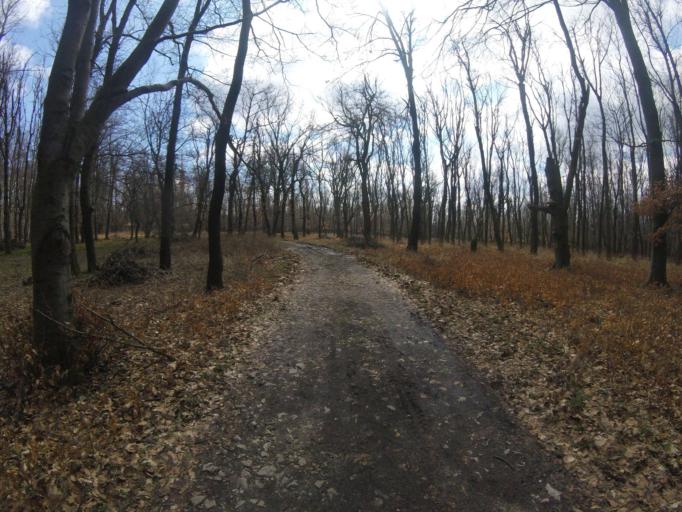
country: HU
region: Komarom-Esztergom
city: Tardos
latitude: 47.6786
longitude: 18.4888
